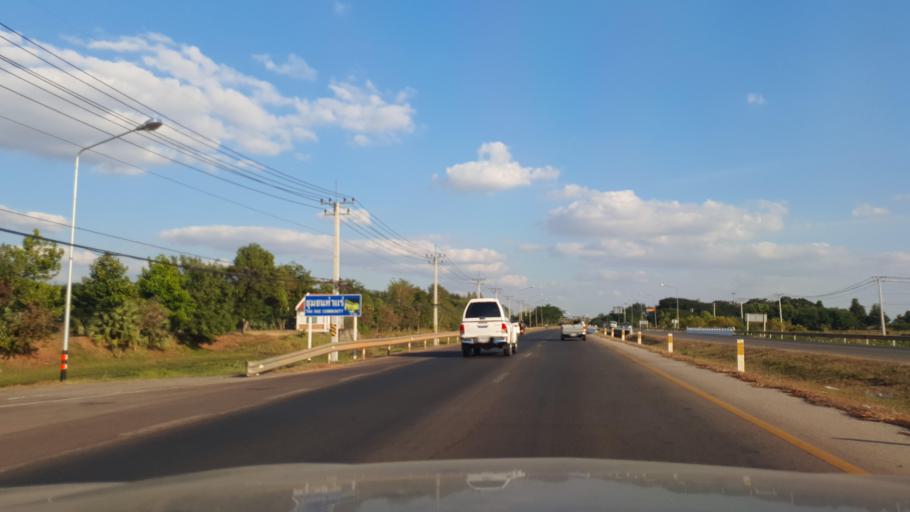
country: TH
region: Sakon Nakhon
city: Sakon Nakhon
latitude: 17.2603
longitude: 104.1558
